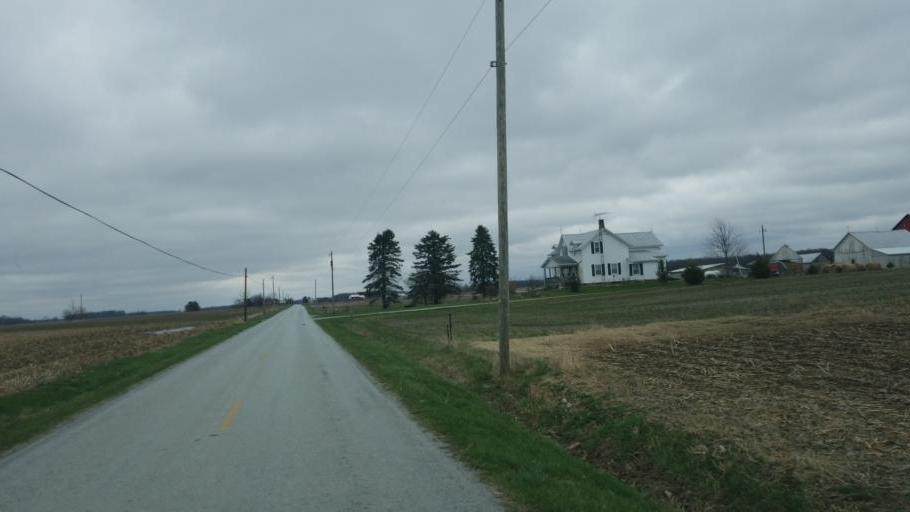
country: US
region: Ohio
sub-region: Hardin County
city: Kenton
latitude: 40.6577
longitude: -83.5037
